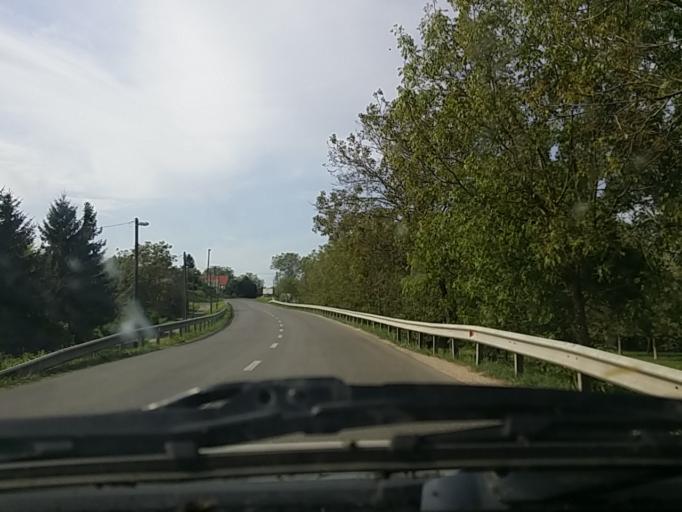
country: HU
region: Baranya
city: Harkany
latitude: 45.9057
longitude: 18.2304
